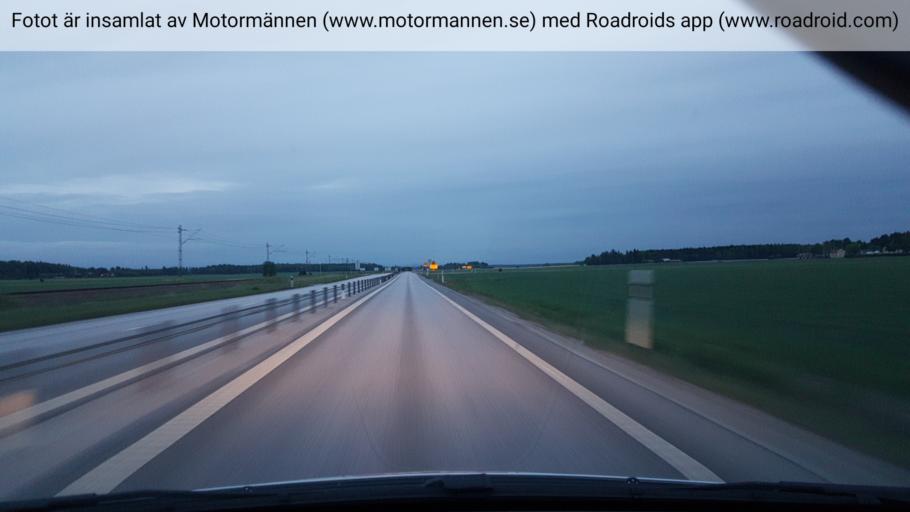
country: SE
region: Vaestmanland
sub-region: Sala Kommun
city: Sala
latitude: 59.8970
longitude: 16.6220
